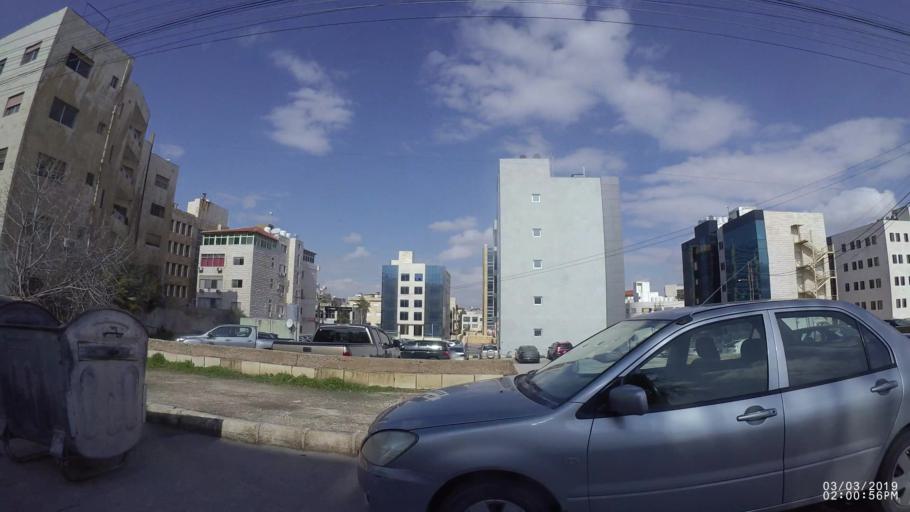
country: JO
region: Amman
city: Amman
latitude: 31.9780
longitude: 35.8944
